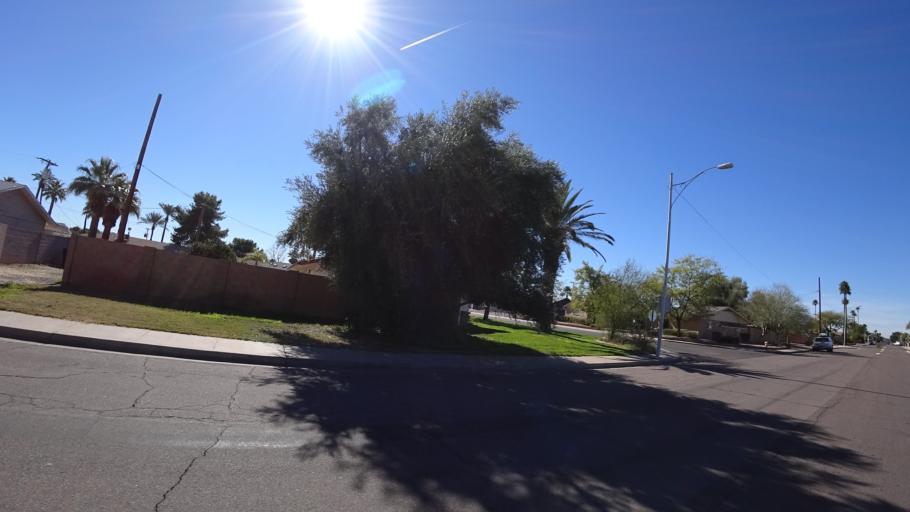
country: US
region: Arizona
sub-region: Maricopa County
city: Scottsdale
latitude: 33.5021
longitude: -111.8969
